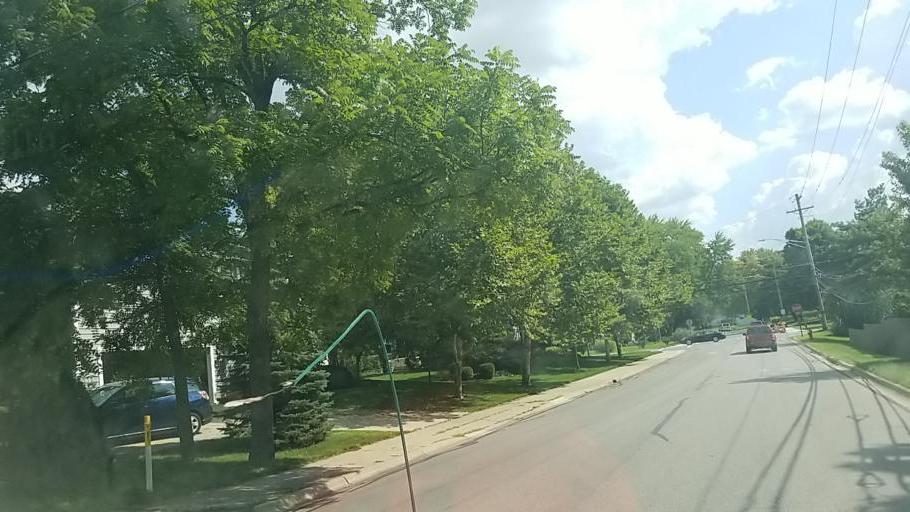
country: US
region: Ohio
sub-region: Franklin County
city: Westerville
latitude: 40.1268
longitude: -82.9218
